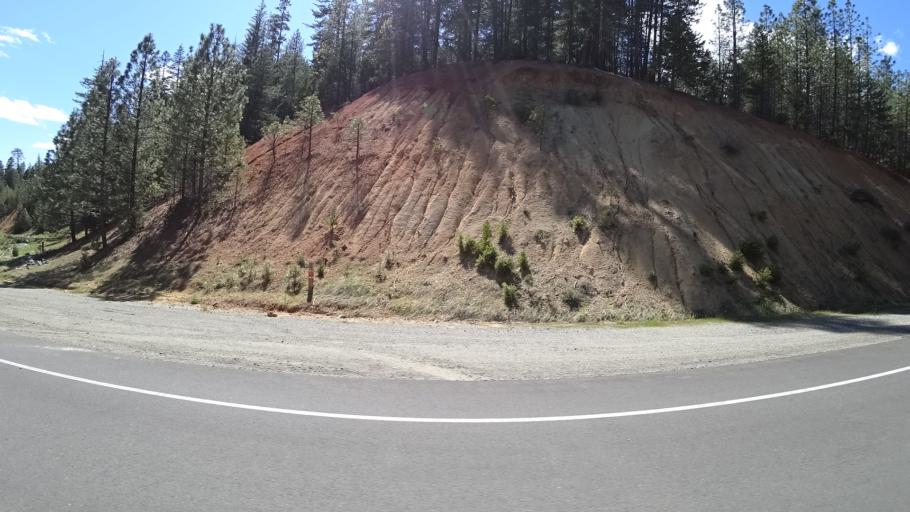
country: US
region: California
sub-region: Trinity County
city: Lewiston
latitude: 40.8763
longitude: -122.8021
